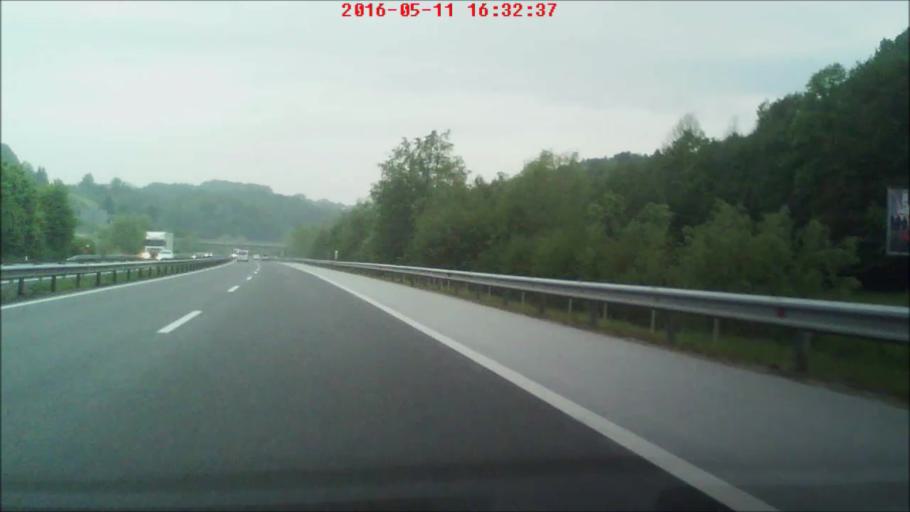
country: SI
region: Kungota
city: Zgornja Kungota
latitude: 46.6429
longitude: 15.6510
